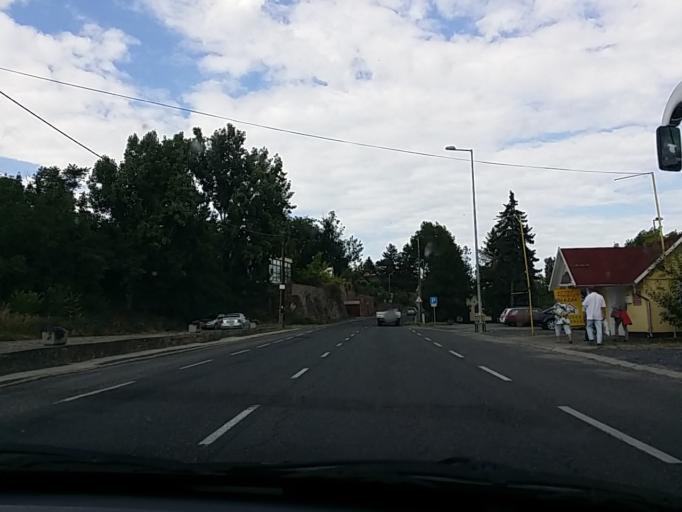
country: HU
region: Veszprem
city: Zanka
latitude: 46.8505
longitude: 17.6619
